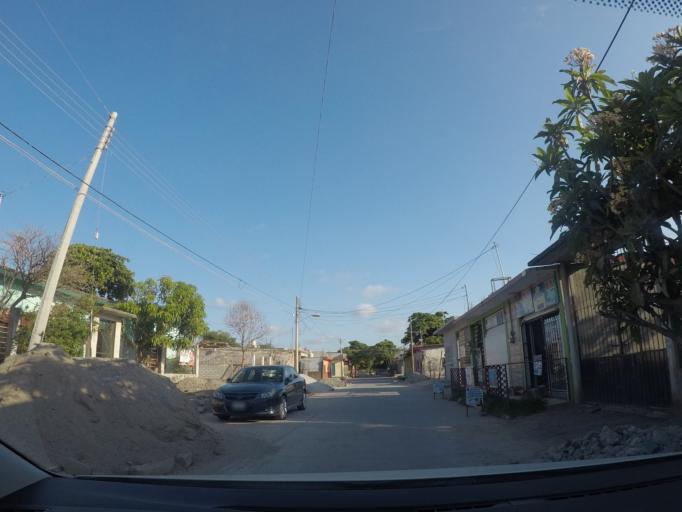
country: MX
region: Oaxaca
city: Juchitan de Zaragoza
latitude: 16.4365
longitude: -95.0290
